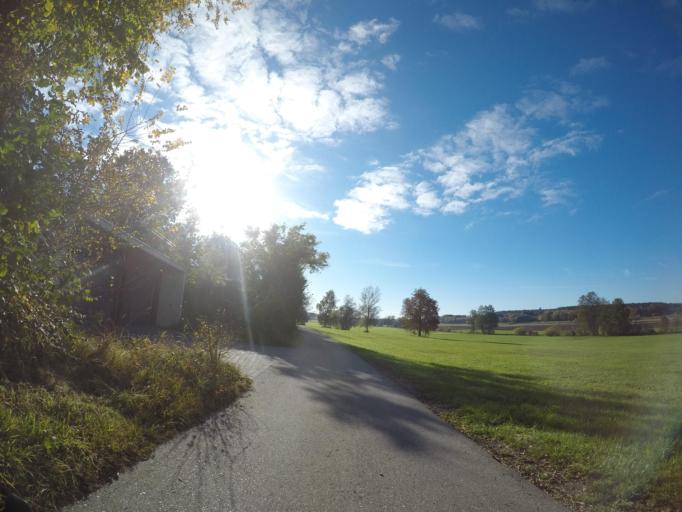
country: DE
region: Baden-Wuerttemberg
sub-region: Tuebingen Region
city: Herbertingen
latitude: 48.0535
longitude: 9.4436
